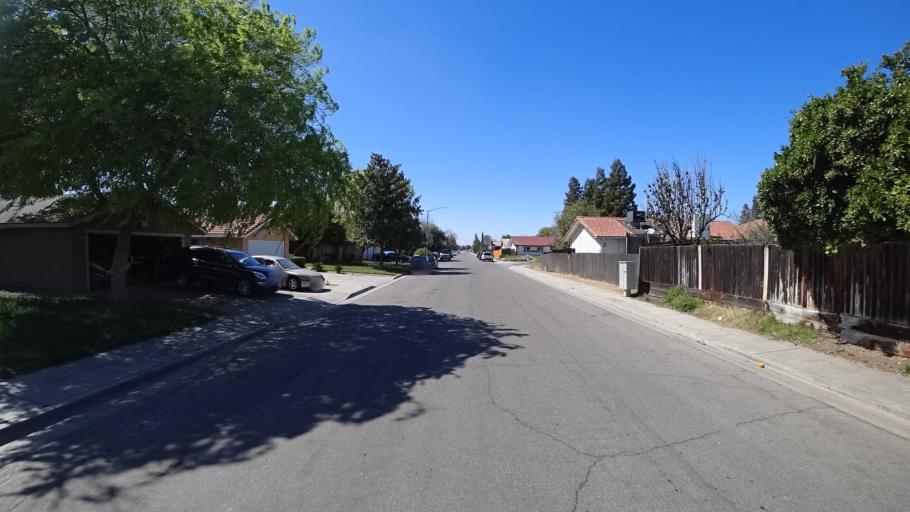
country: US
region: California
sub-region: Fresno County
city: West Park
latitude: 36.7885
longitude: -119.8634
